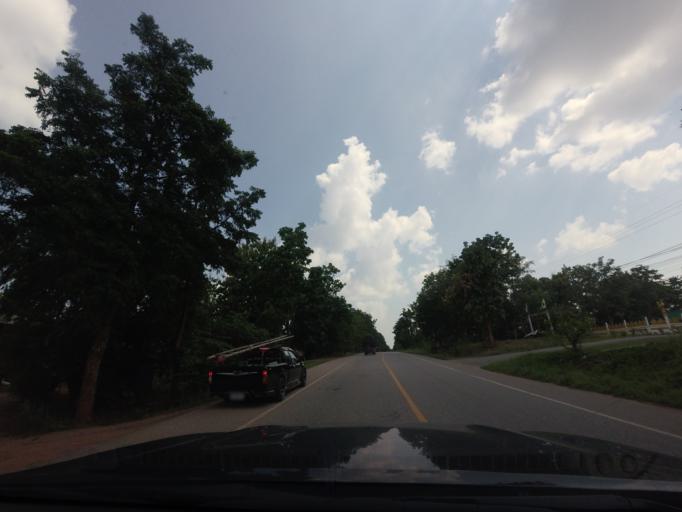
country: TH
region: Phitsanulok
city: Chat Trakan
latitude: 17.2794
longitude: 100.5379
